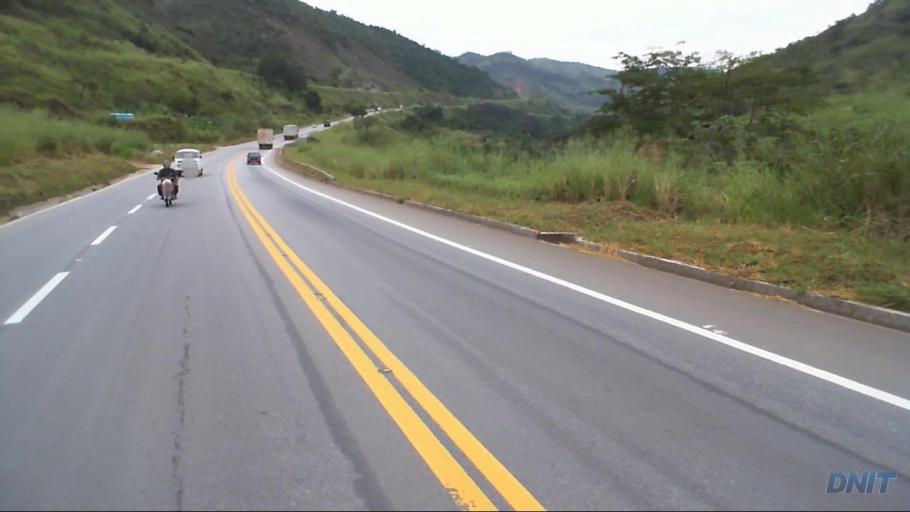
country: BR
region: Minas Gerais
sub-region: Timoteo
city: Timoteo
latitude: -19.6264
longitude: -42.8061
